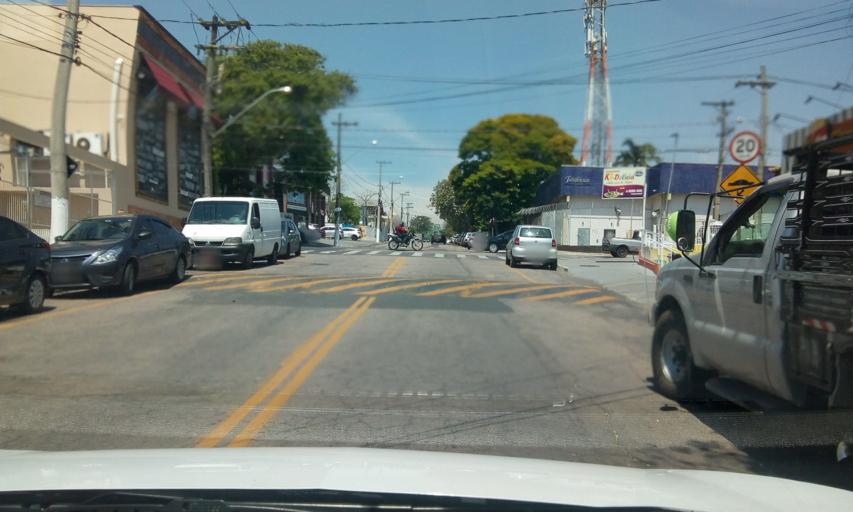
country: BR
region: Sao Paulo
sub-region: Itupeva
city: Itupeva
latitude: -23.1550
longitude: -47.0589
